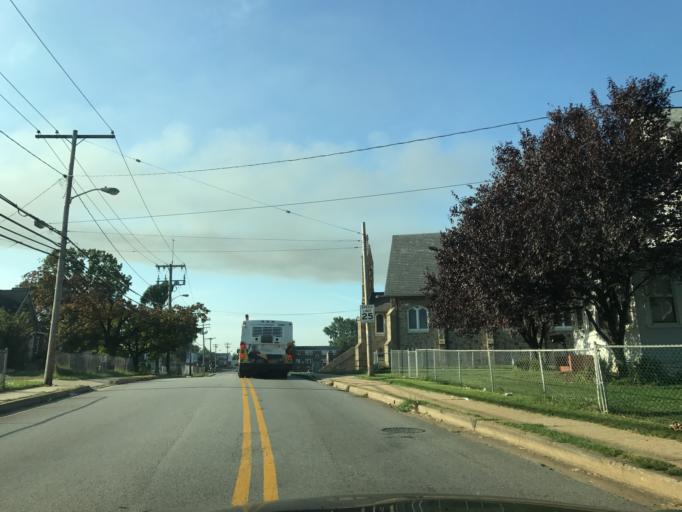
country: US
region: Maryland
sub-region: Baltimore County
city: Lansdowne
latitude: 39.2549
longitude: -76.6465
